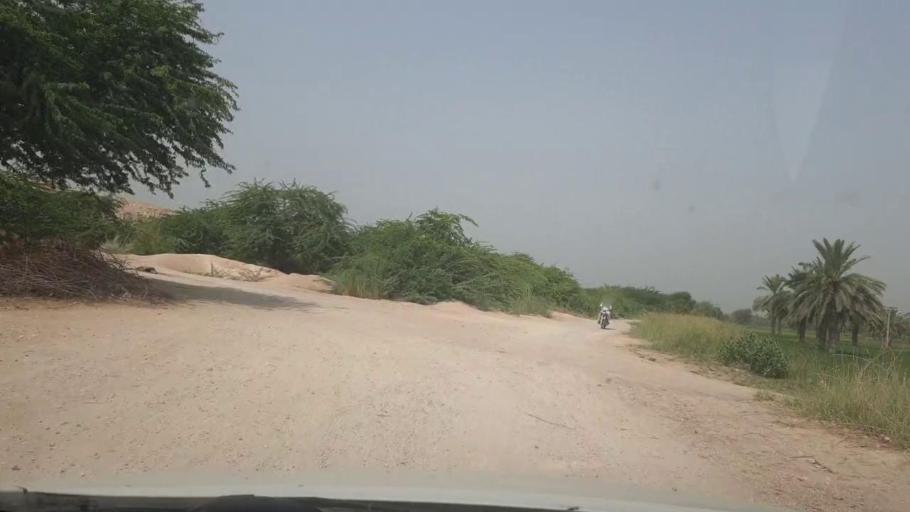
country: PK
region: Sindh
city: Kot Diji
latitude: 27.3069
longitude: 68.6897
